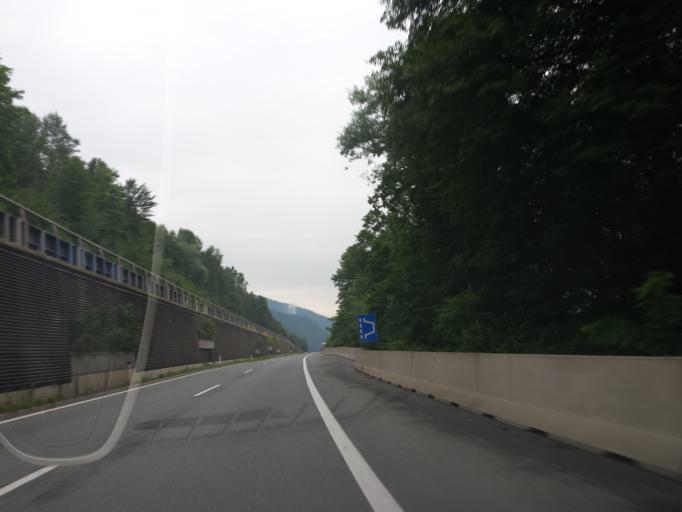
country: AT
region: Styria
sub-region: Politischer Bezirk Graz-Umgebung
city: Rothelstein
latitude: 47.3184
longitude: 15.3683
